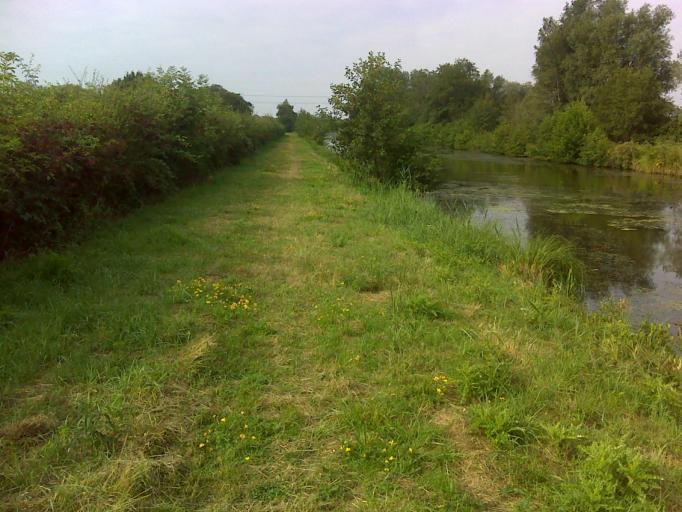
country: FR
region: Nord-Pas-de-Calais
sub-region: Departement du Nord
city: Landrecies
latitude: 50.1207
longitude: 3.6796
